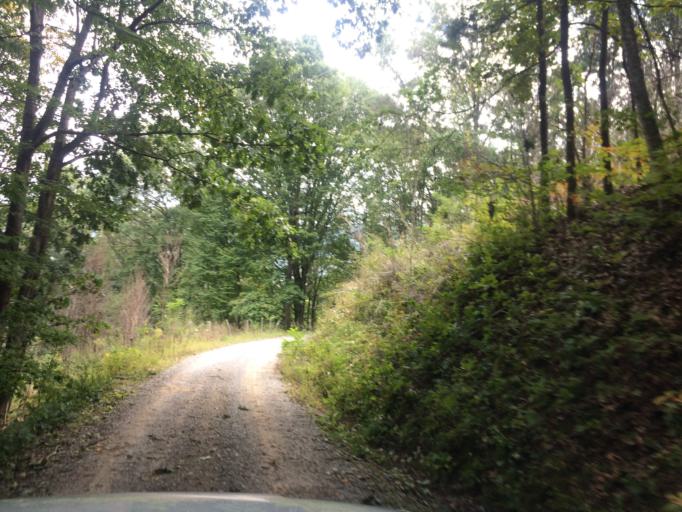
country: US
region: North Carolina
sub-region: Haywood County
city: Clyde
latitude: 35.5558
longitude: -82.9138
